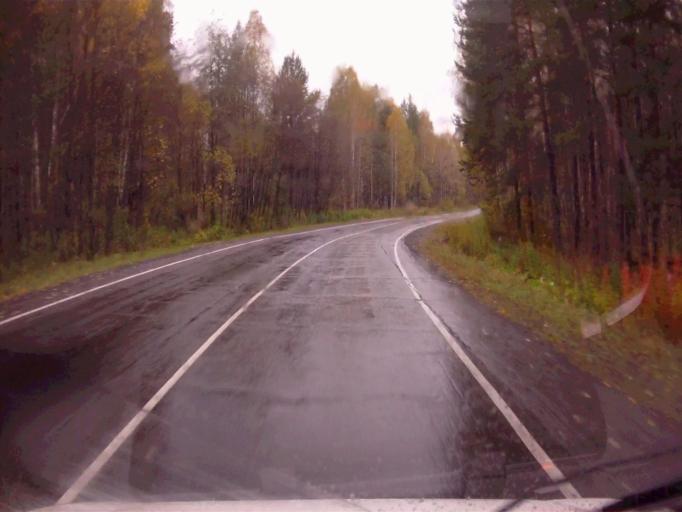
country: RU
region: Chelyabinsk
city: Verkhniy Ufaley
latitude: 55.9528
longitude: 60.3946
